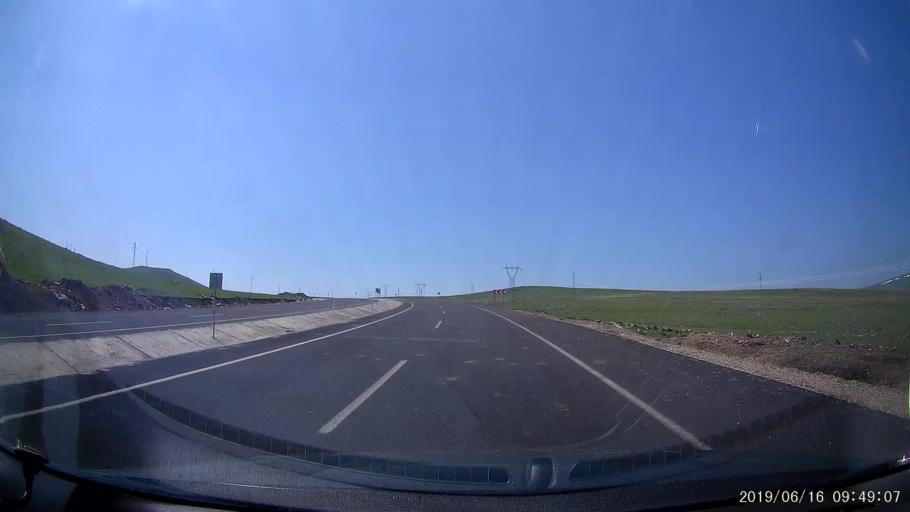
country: TR
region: Kars
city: Digor
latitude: 40.4251
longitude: 43.3564
